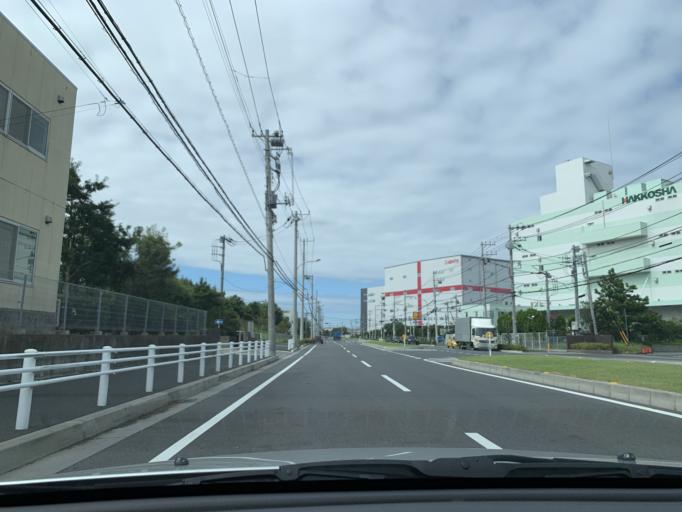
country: JP
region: Tokyo
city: Urayasu
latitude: 35.6227
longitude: 139.8994
